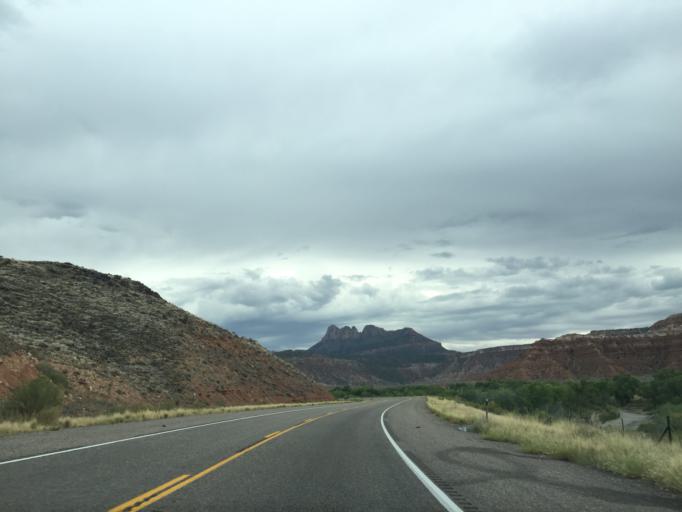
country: US
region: Utah
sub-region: Washington County
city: LaVerkin
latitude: 37.1767
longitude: -113.1153
